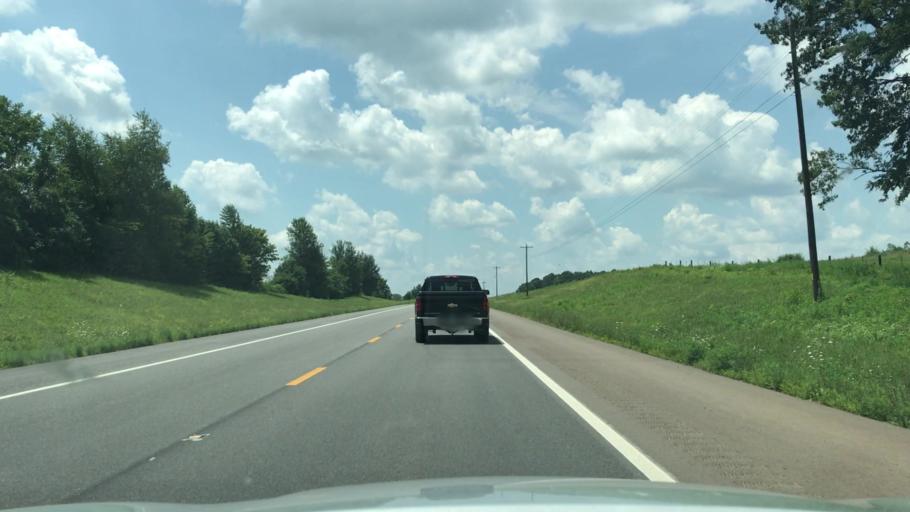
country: US
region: Tennessee
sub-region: Pickett County
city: Byrdstown
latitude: 36.5061
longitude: -85.1746
